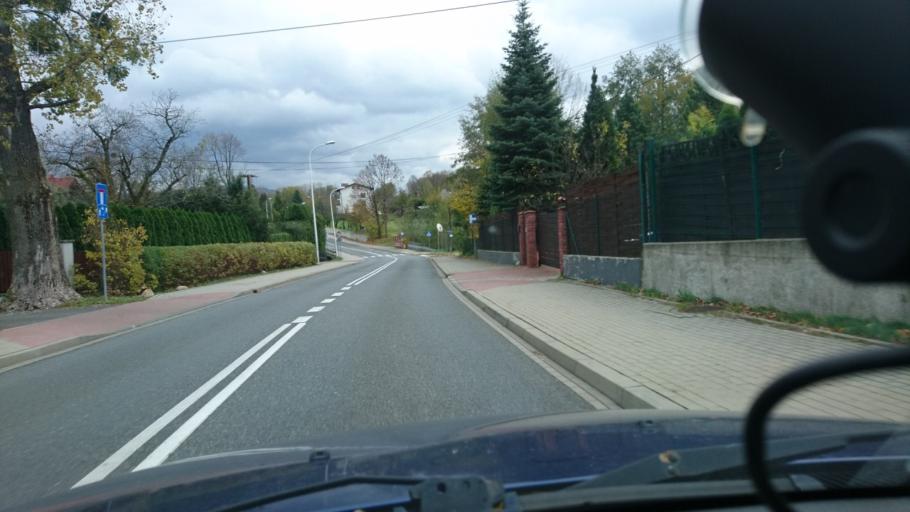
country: PL
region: Silesian Voivodeship
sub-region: Bielsko-Biala
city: Bielsko-Biala
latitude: 49.7933
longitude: 19.0266
